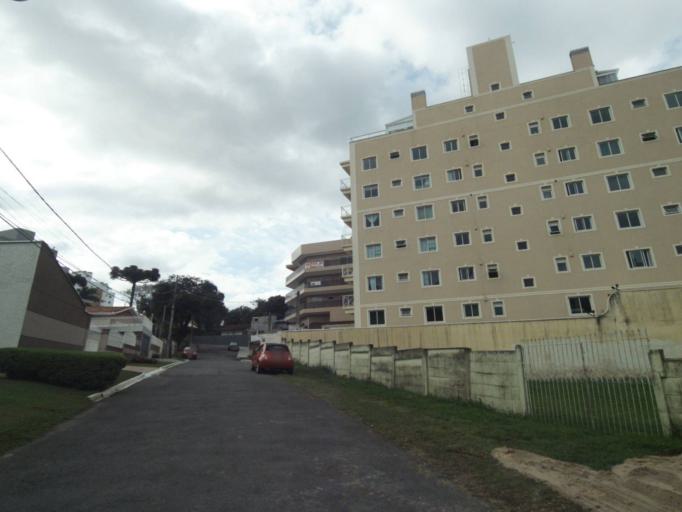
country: BR
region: Parana
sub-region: Curitiba
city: Curitiba
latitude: -25.4046
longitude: -49.2613
